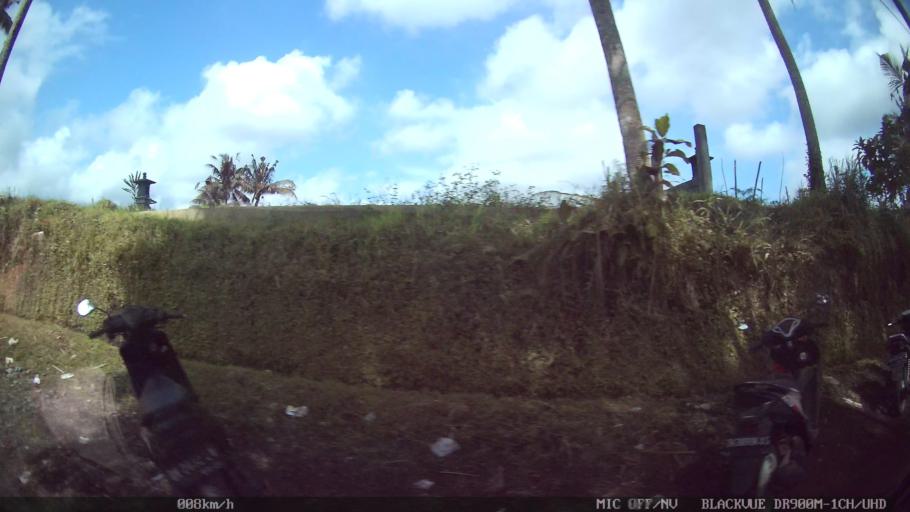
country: ID
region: Bali
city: Banjar Pesalakan
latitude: -8.5101
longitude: 115.3062
